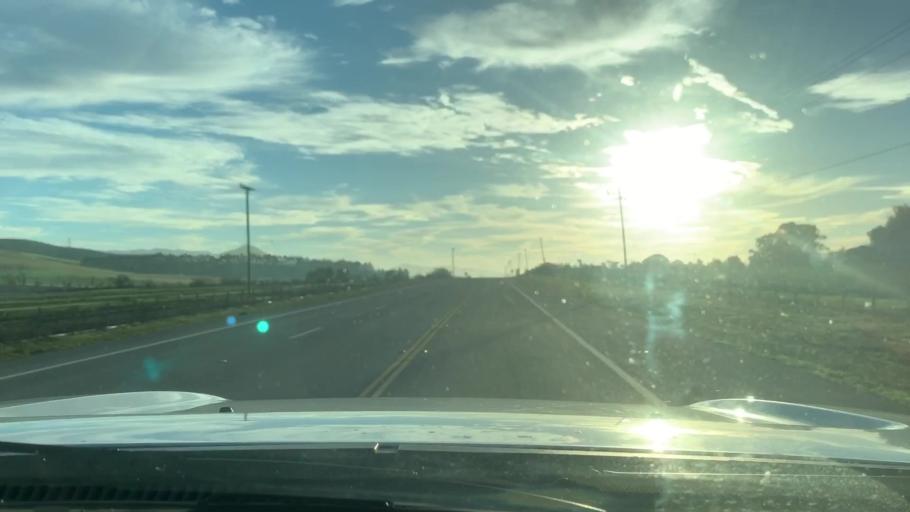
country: US
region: California
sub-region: San Luis Obispo County
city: San Luis Obispo
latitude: 35.2894
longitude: -120.7462
